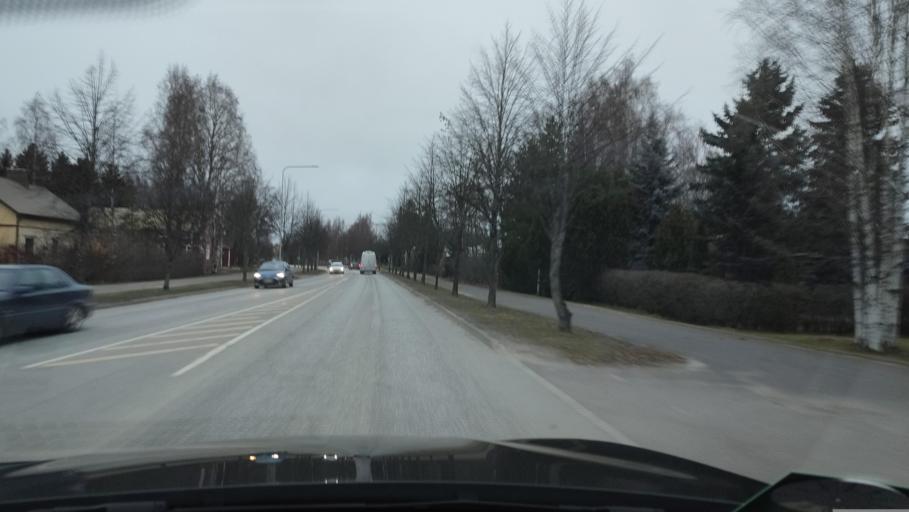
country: FI
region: Southern Ostrobothnia
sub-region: Suupohja
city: Kauhajoki
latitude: 62.4184
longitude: 22.1759
